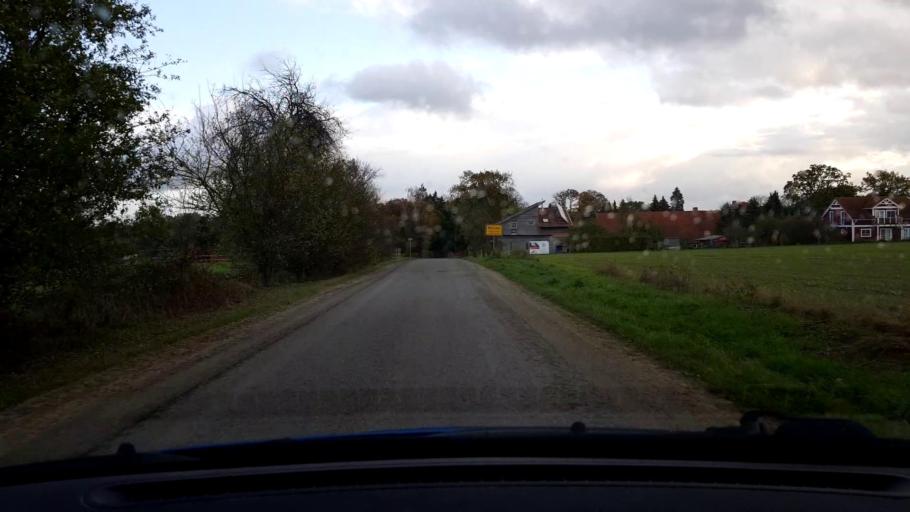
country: DE
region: Lower Saxony
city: Reinstorf
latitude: 53.2439
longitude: 10.5792
